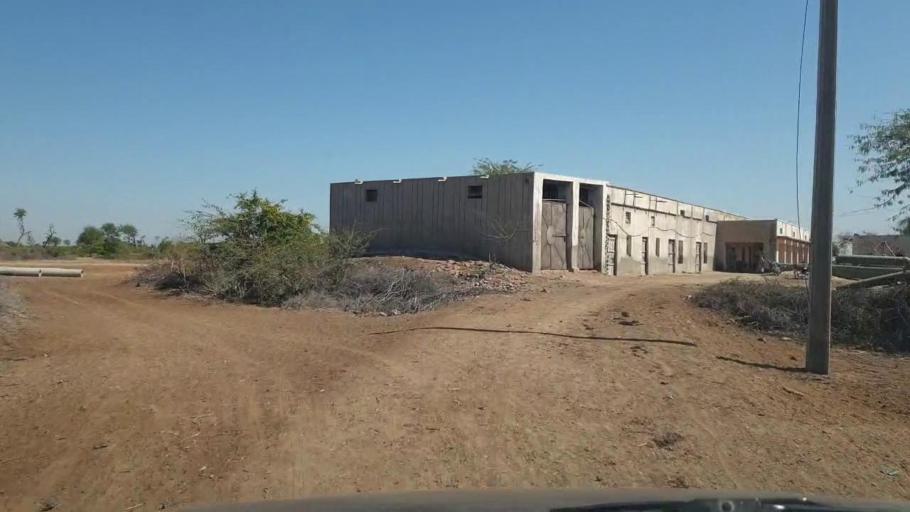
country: PK
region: Sindh
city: Dhoro Naro
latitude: 25.4224
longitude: 69.6444
